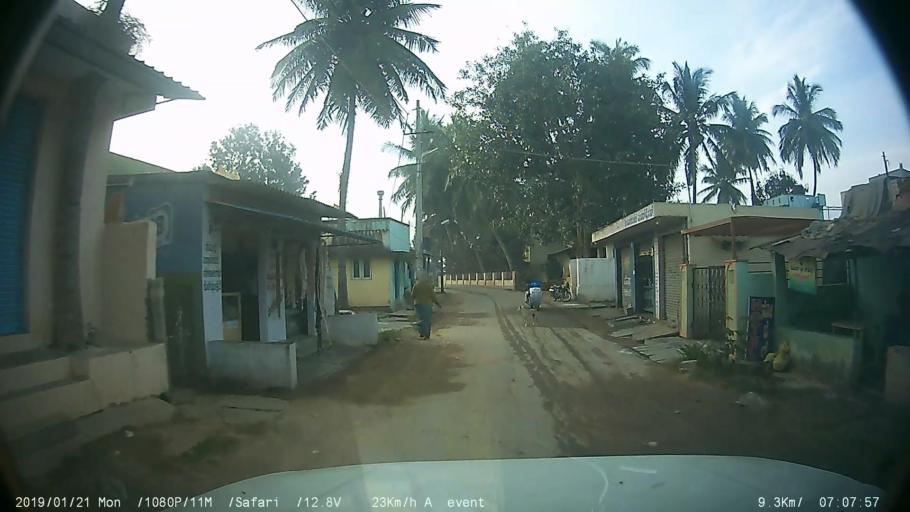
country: IN
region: Karnataka
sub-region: Bangalore Urban
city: Anekal
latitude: 12.8187
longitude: 77.6373
